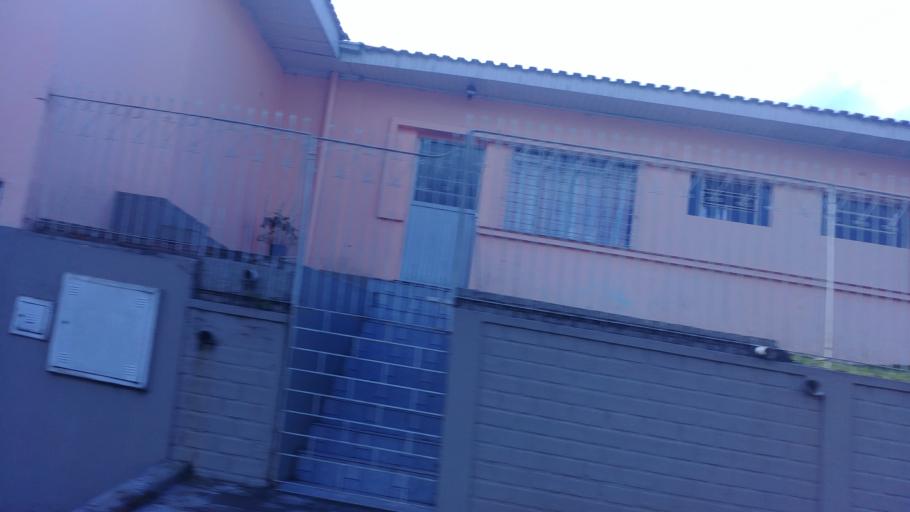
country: BR
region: Parana
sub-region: Guarapuava
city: Guarapuava
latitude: -25.3865
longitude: -51.4656
